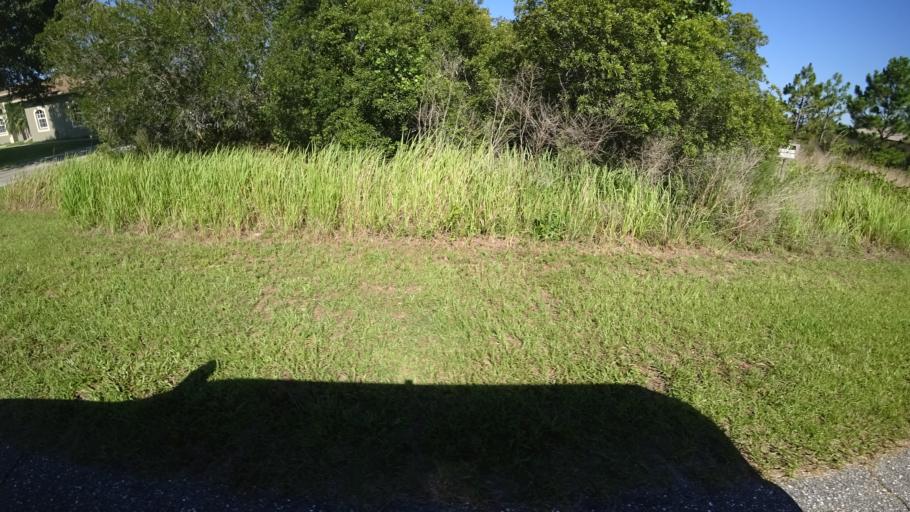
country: US
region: Florida
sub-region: Sarasota County
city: Fruitville
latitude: 27.3987
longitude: -82.3013
